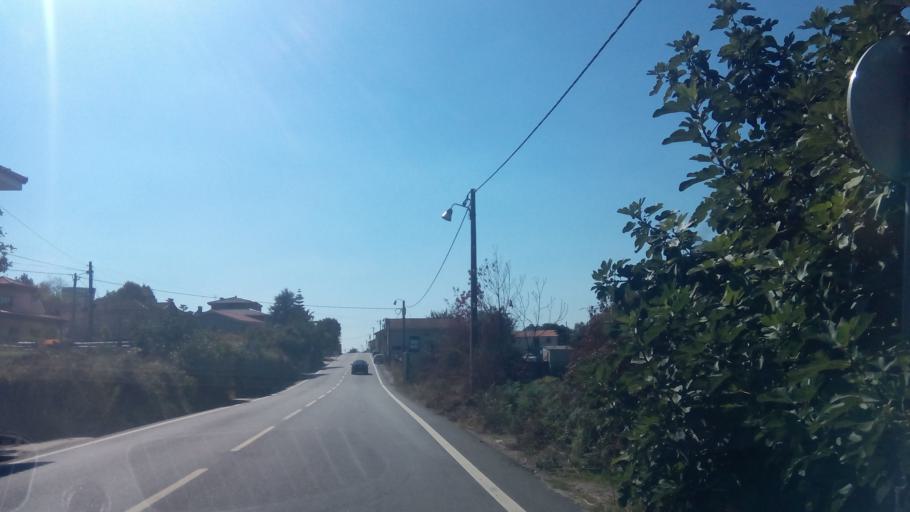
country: PT
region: Porto
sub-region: Lousada
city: Meinedo
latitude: 41.2373
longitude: -8.2224
